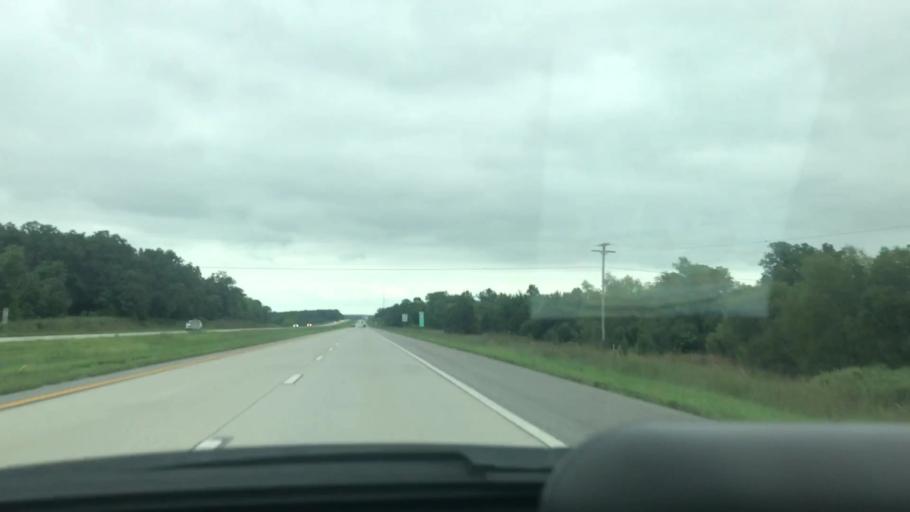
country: US
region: Missouri
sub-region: Greene County
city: Fair Grove
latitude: 37.4881
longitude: -93.1391
